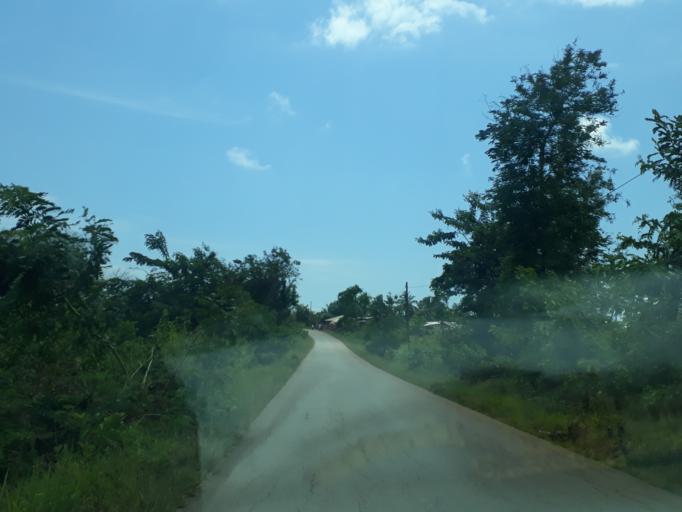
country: TZ
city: Kiwengwa
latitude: -5.9947
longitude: 39.3441
